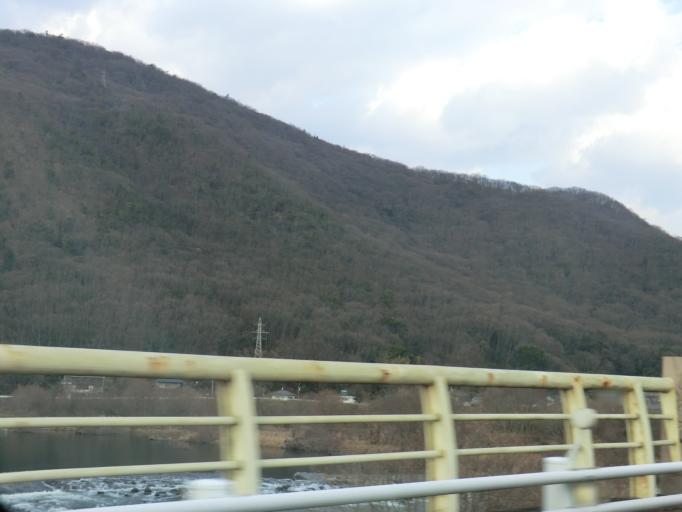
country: JP
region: Okayama
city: Okayama-shi
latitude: 34.7209
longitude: 133.9702
